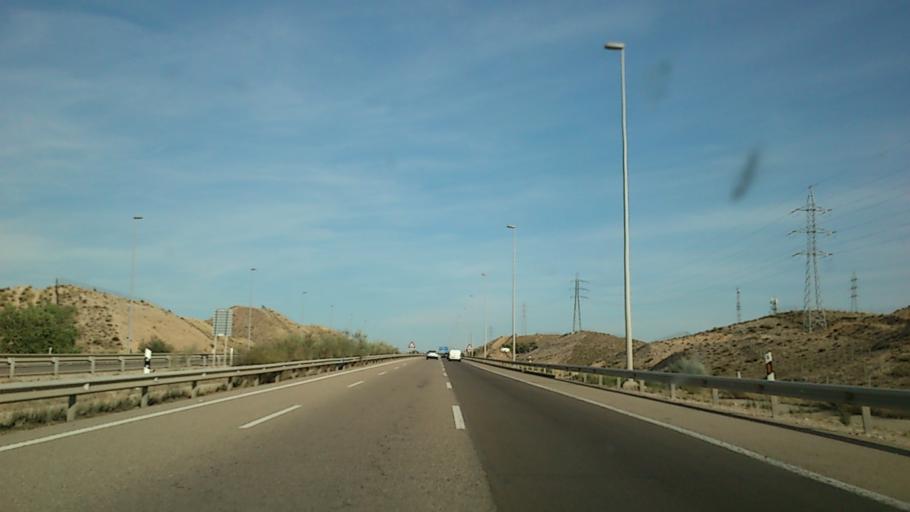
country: ES
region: Aragon
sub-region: Provincia de Zaragoza
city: Cuarte de Huerva
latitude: 41.6079
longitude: -0.9127
